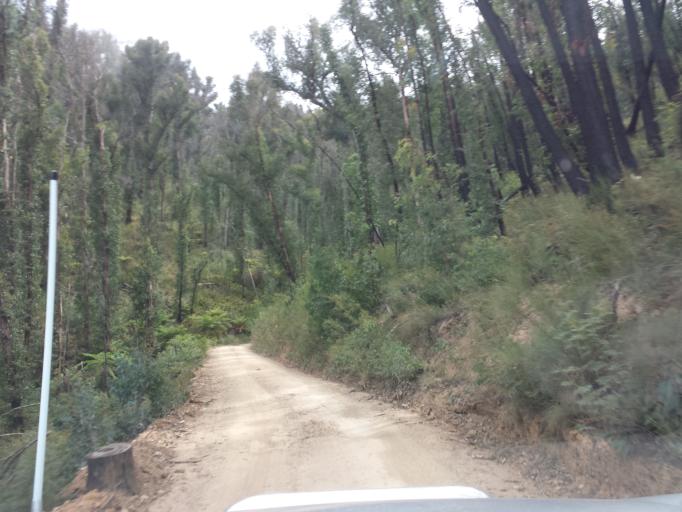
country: AU
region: Victoria
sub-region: Wellington
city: Heyfield
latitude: -37.7443
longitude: 146.4091
